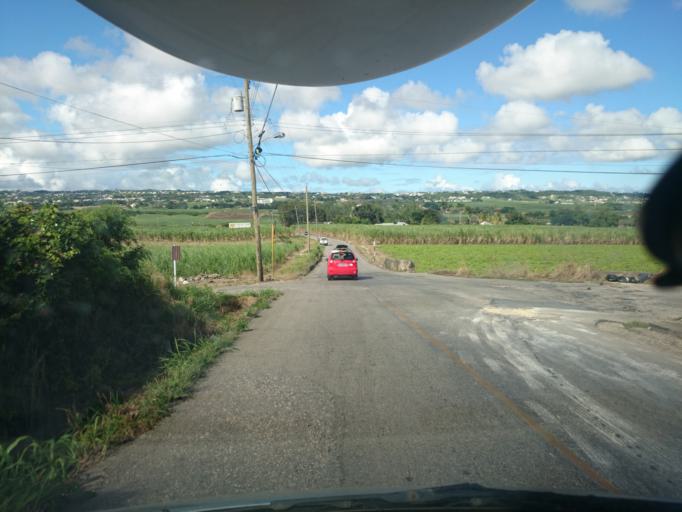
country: BB
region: Christ Church
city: Oistins
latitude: 13.1055
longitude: -59.5286
